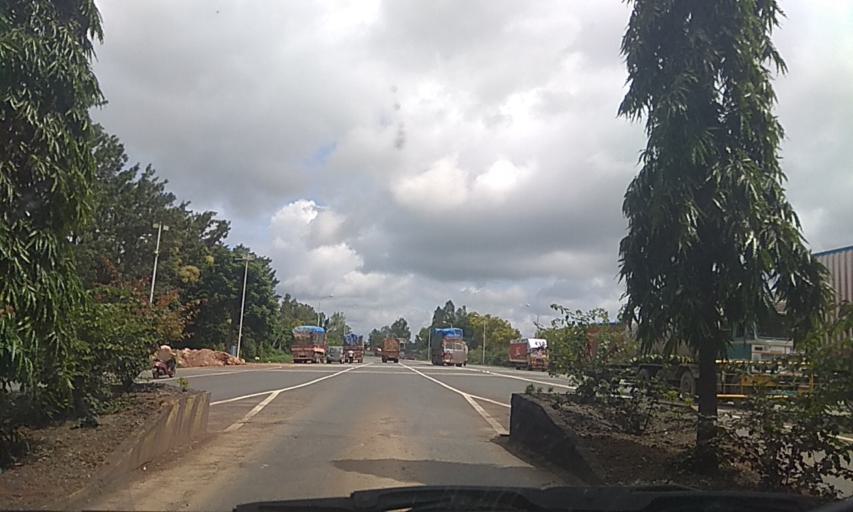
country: IN
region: Karnataka
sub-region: Dharwad
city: Hubli
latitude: 15.4888
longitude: 74.9695
